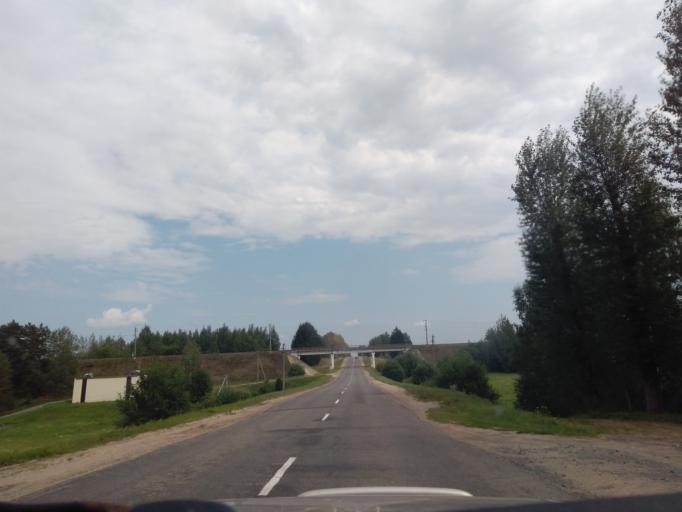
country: BY
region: Minsk
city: Khatsyezhyna
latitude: 53.9131
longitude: 27.3203
